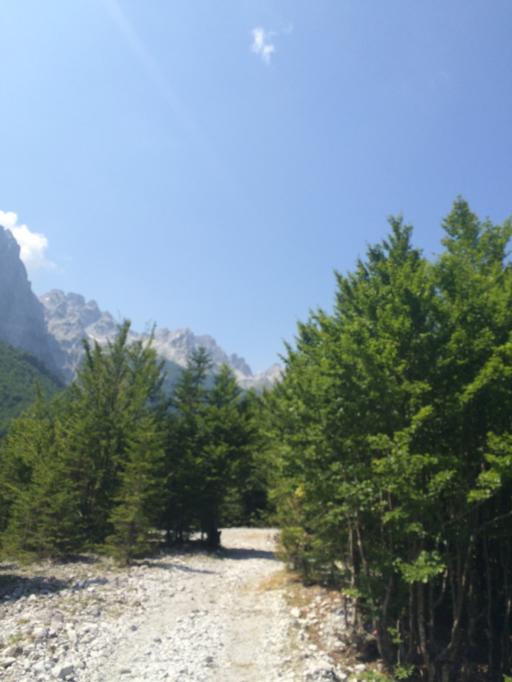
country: AL
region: Kukes
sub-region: Rrethi i Tropojes
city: Valbone
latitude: 42.4228
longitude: 19.8686
